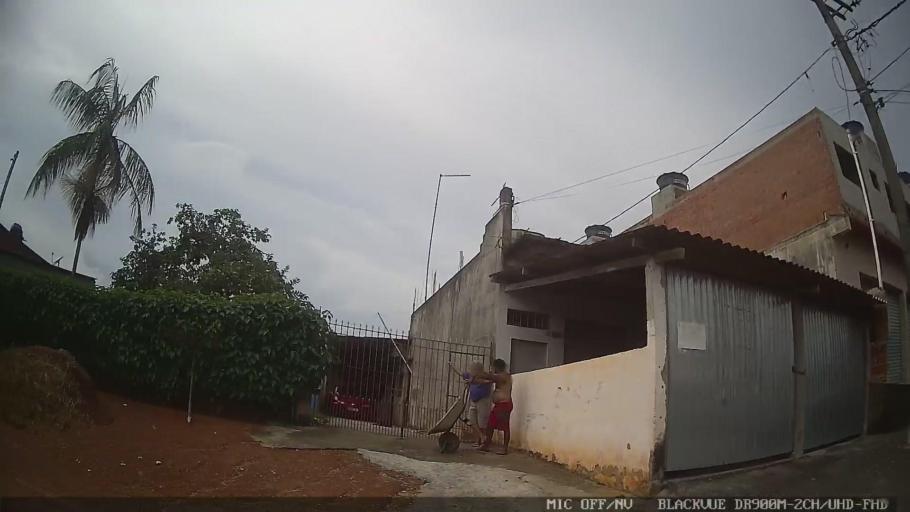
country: BR
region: Sao Paulo
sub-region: Aruja
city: Aruja
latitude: -23.4387
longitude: -46.2762
